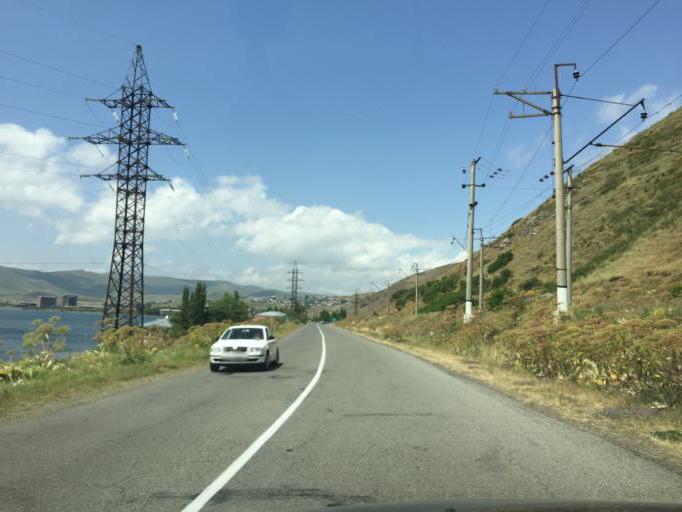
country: AM
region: Geghark'unik'i Marz
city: Tsovagyugh
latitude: 40.6306
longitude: 44.9973
